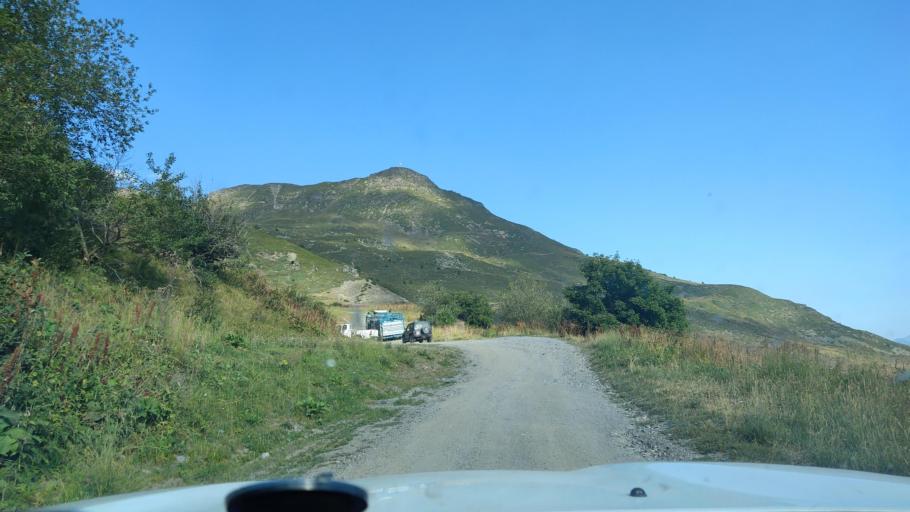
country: FR
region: Rhone-Alpes
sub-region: Departement de la Savoie
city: Val Thorens
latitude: 45.3203
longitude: 6.5285
